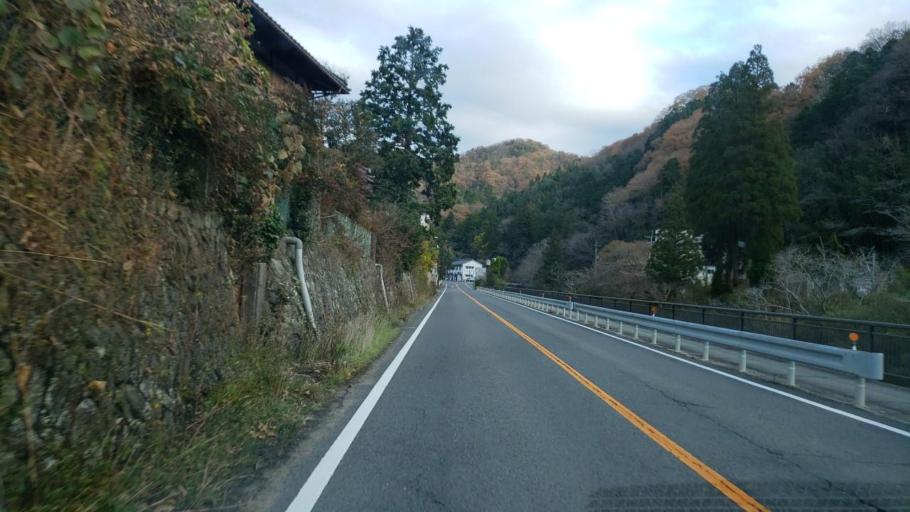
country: JP
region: Tokushima
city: Wakimachi
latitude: 34.1693
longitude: 134.0836
